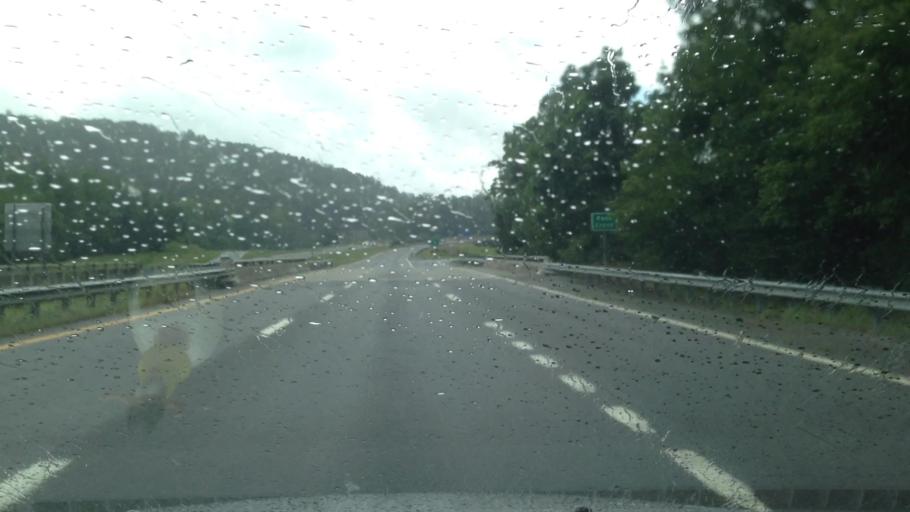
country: US
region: Virginia
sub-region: Henry County
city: Collinsville
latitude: 36.7299
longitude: -79.9378
